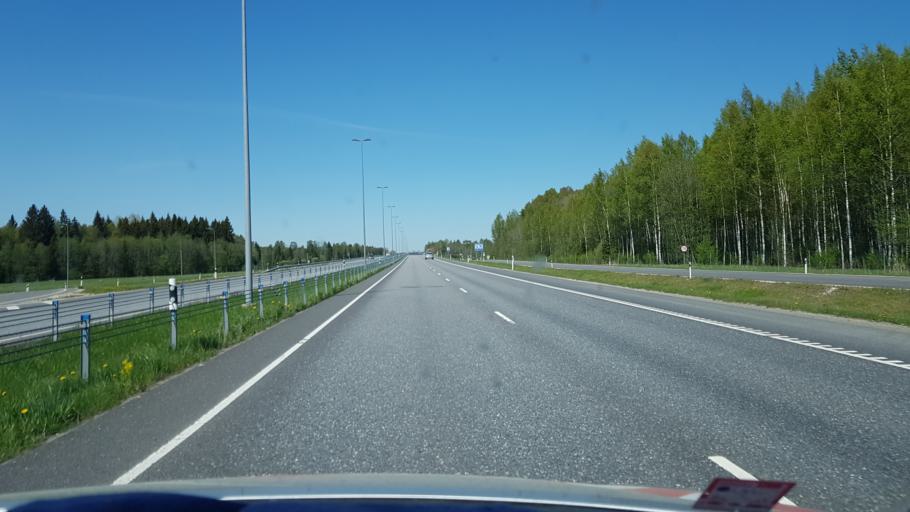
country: EE
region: Harju
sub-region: Rae vald
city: Vaida
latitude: 59.2146
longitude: 25.0369
